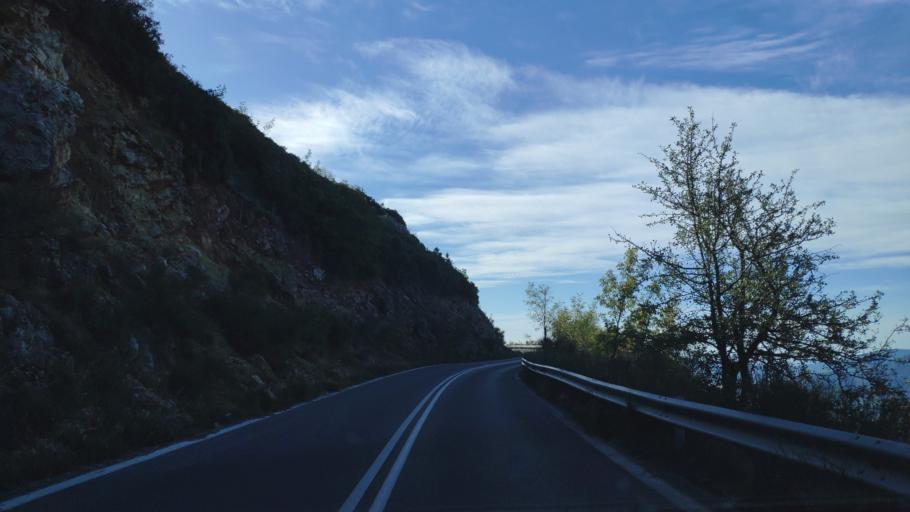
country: GR
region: Peloponnese
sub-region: Nomos Arkadias
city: Dimitsana
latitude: 37.5512
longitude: 22.0650
